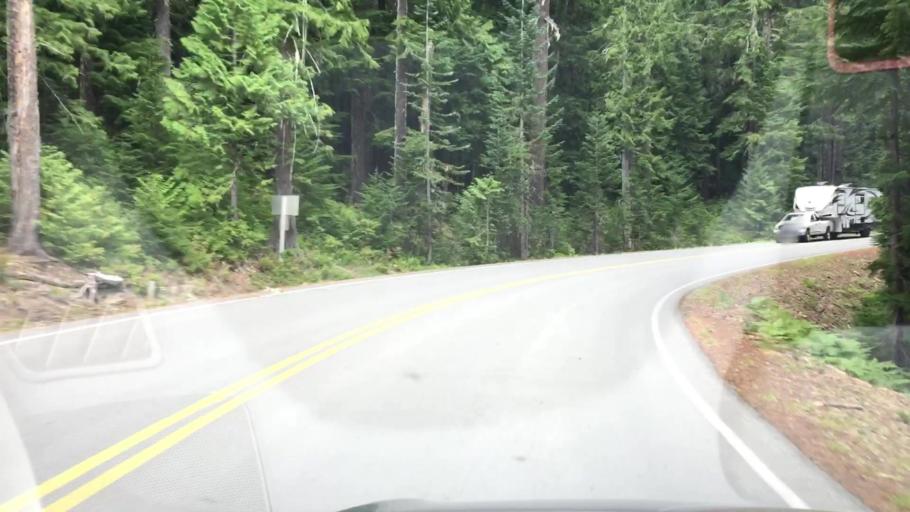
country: US
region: Washington
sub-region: Klickitat County
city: White Salmon
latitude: 46.1429
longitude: -121.6283
